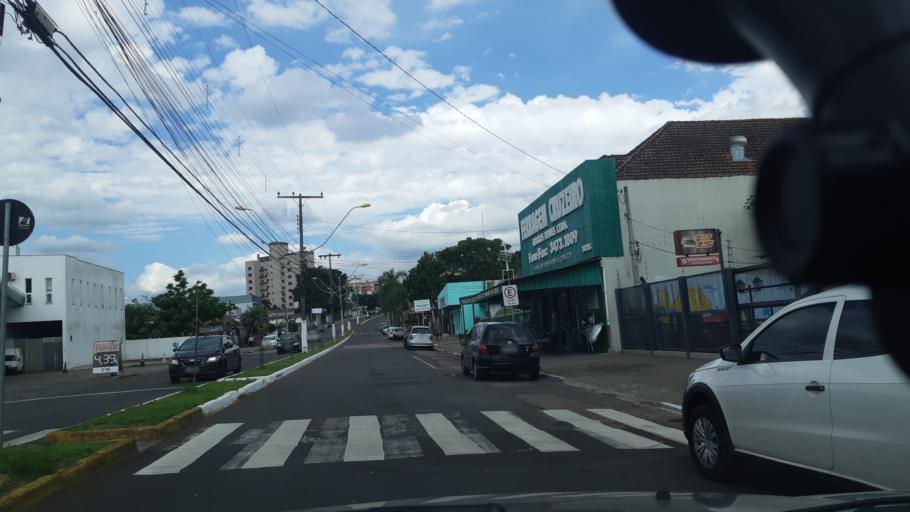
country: BR
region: Rio Grande do Sul
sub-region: Esteio
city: Esteio
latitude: -29.8492
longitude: -51.1654
